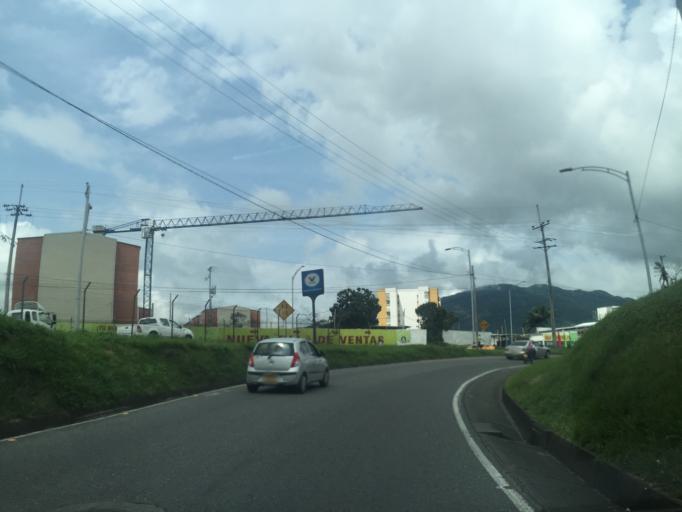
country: CO
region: Risaralda
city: Pereira
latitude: 4.8223
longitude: -75.6851
